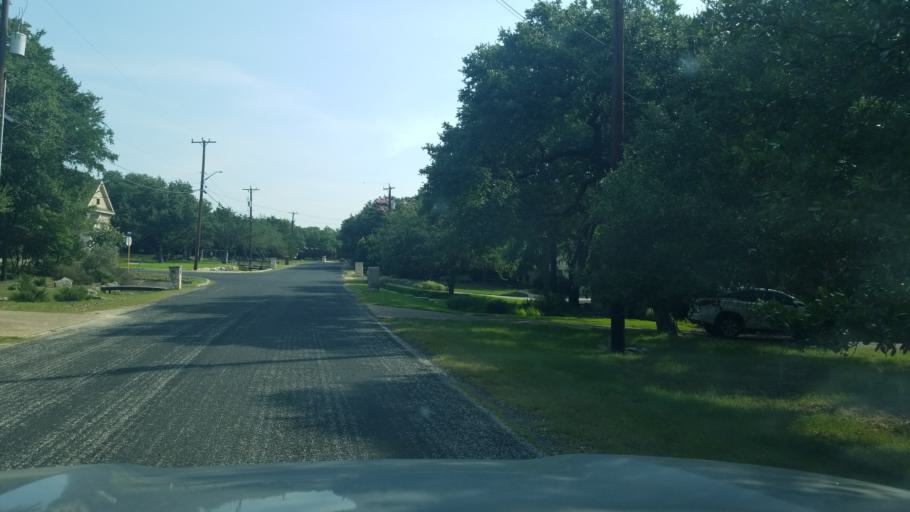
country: US
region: Texas
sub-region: Bexar County
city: Timberwood Park
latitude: 29.6948
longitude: -98.4991
